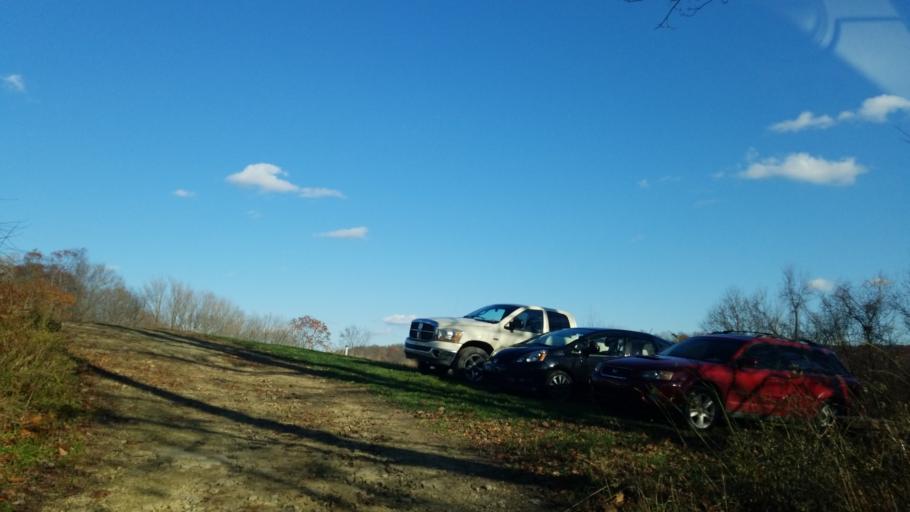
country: US
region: Pennsylvania
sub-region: Clearfield County
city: Treasure Lake
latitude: 41.1564
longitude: -78.6553
